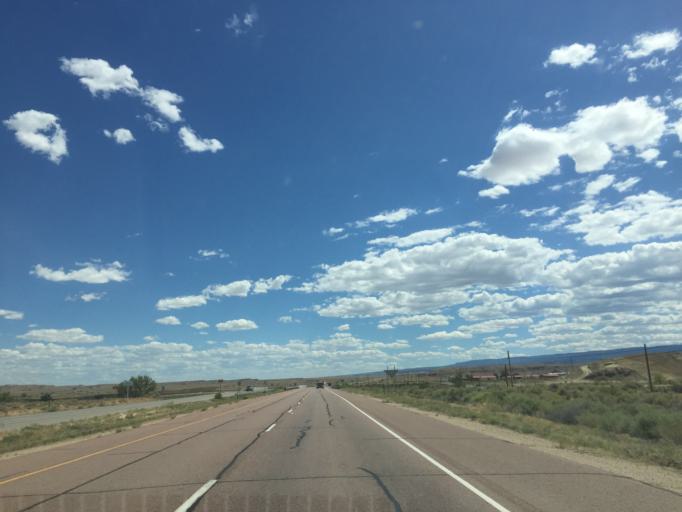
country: US
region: New Mexico
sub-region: San Juan County
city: Shiprock
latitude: 36.2889
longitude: -108.7056
